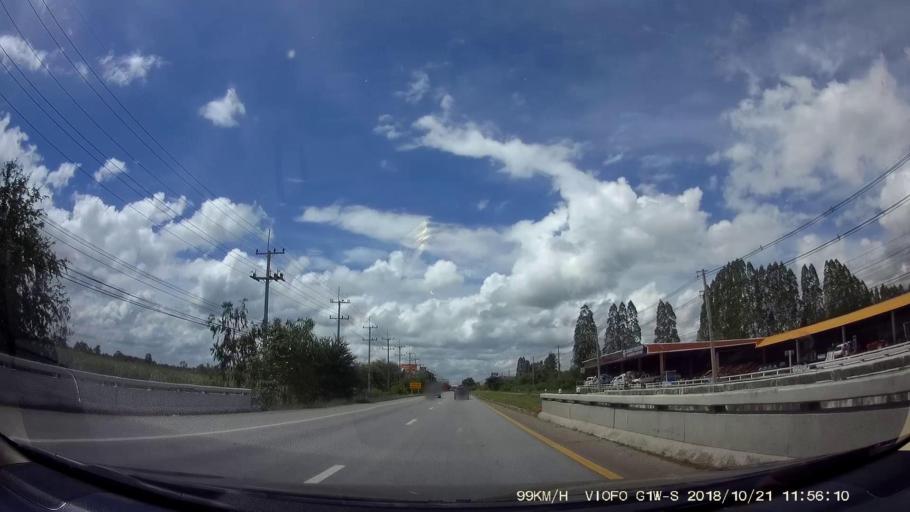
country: TH
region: Chaiyaphum
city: Chatturat
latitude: 15.5782
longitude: 101.8795
